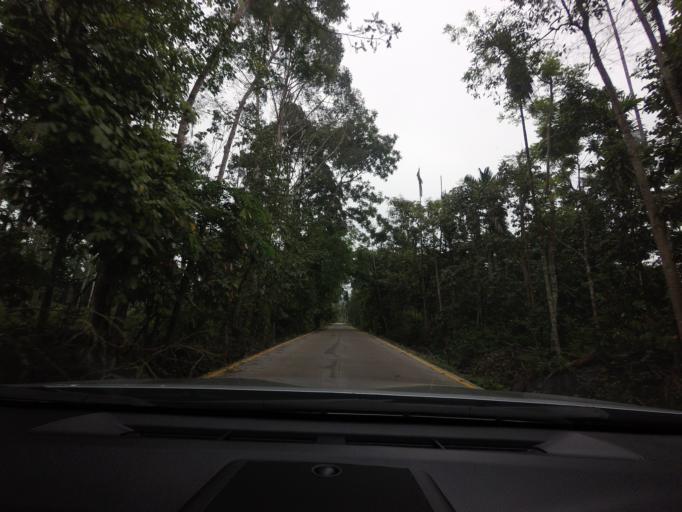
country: TH
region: Narathiwat
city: Rueso
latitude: 6.4131
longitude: 101.5264
